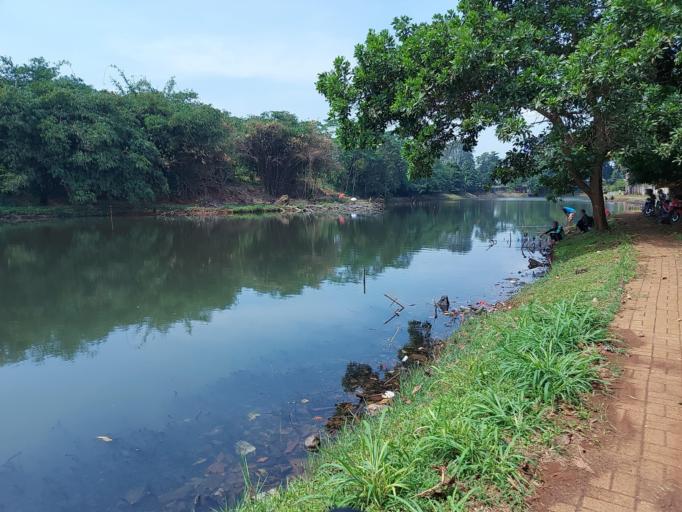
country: ID
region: West Java
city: Cibinong
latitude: -6.4811
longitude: 106.8330
